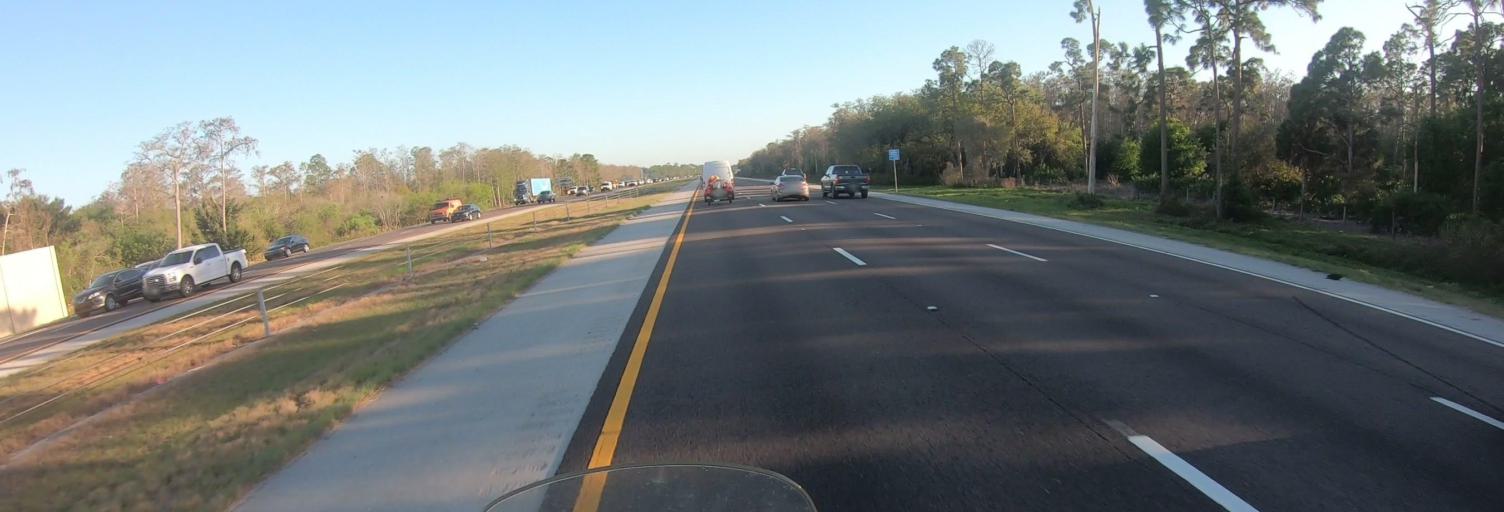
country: US
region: Florida
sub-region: Lee County
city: Bonita Springs
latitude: 26.3172
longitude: -81.7459
